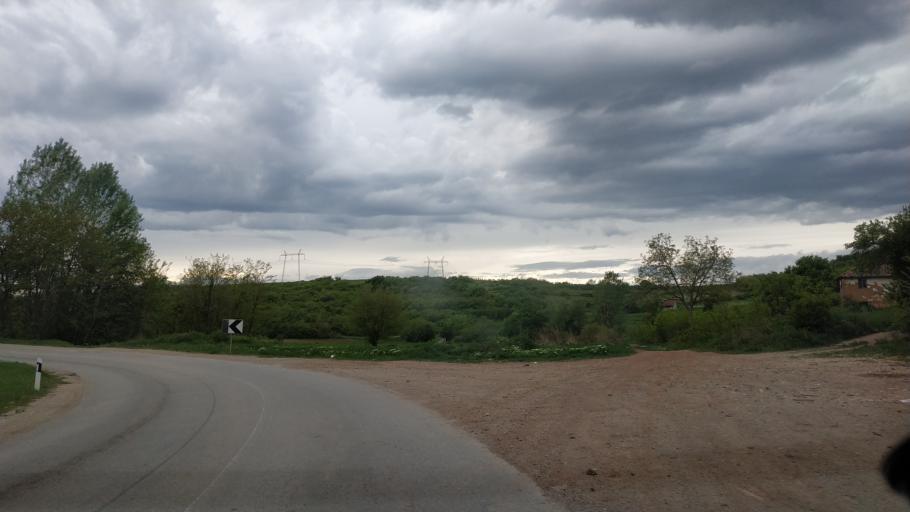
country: RS
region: Central Serbia
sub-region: Nisavski Okrug
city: Aleksinac
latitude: 43.6256
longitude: 21.6926
